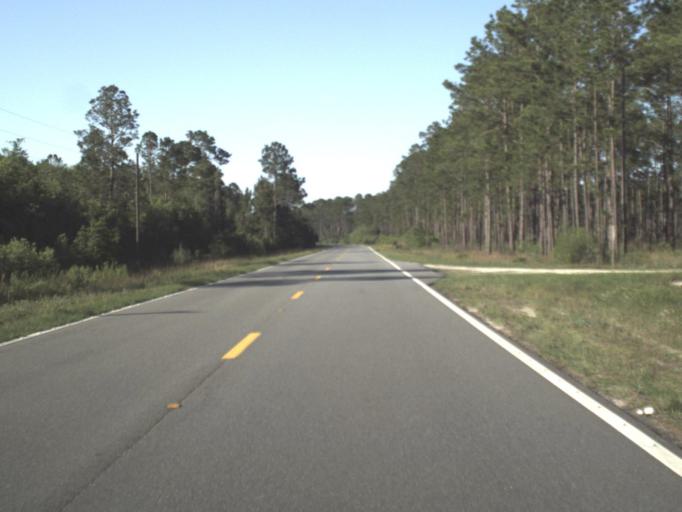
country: US
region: Florida
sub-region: Liberty County
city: Bristol
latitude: 30.2913
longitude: -84.8356
